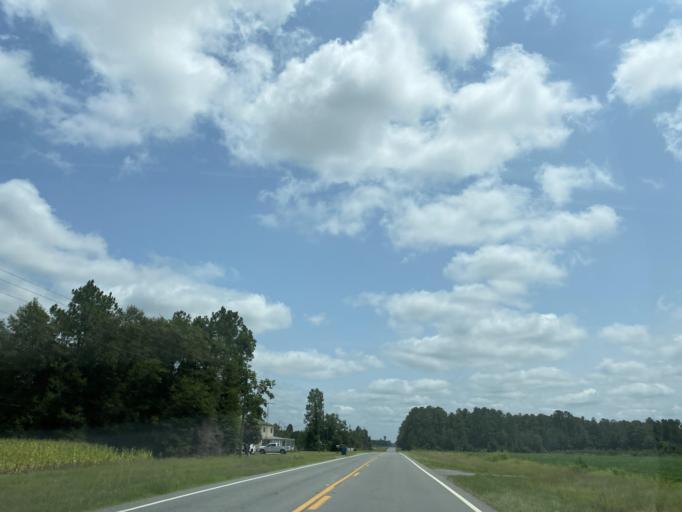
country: US
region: Georgia
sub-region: Bacon County
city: Alma
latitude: 31.6814
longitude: -82.4986
